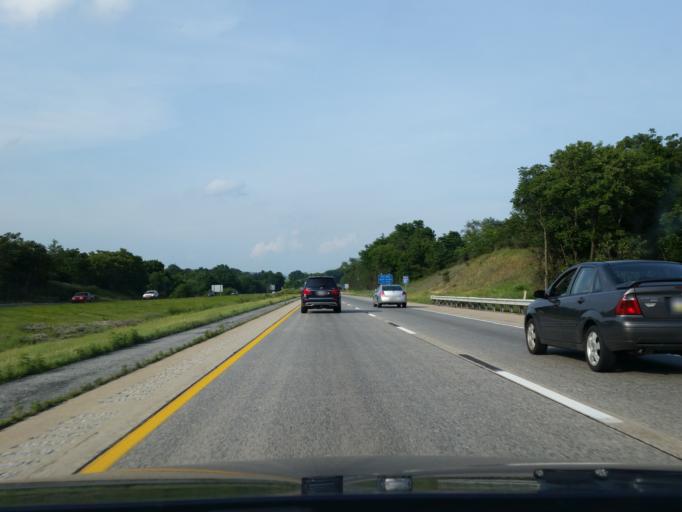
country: US
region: Pennsylvania
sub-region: Dauphin County
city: Skyline View
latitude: 40.3590
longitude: -76.7116
